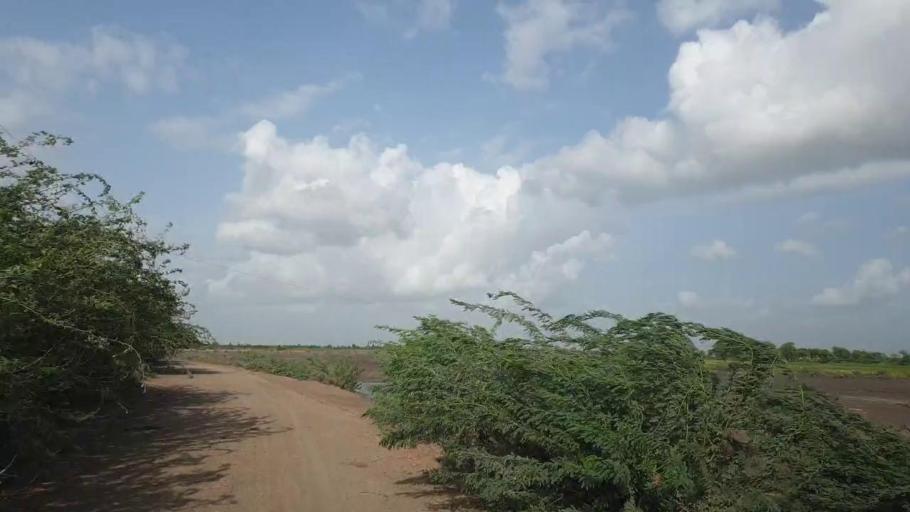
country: PK
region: Sindh
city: Kadhan
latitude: 24.6294
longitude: 69.0828
